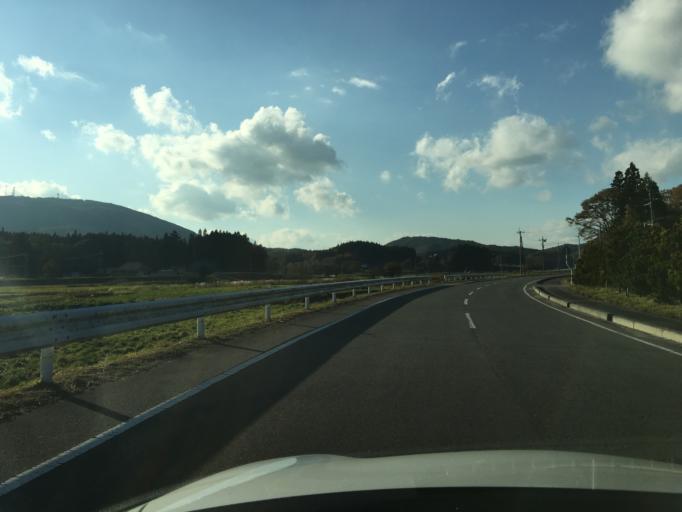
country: JP
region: Fukushima
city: Funehikimachi-funehiki
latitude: 37.2925
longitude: 140.7174
